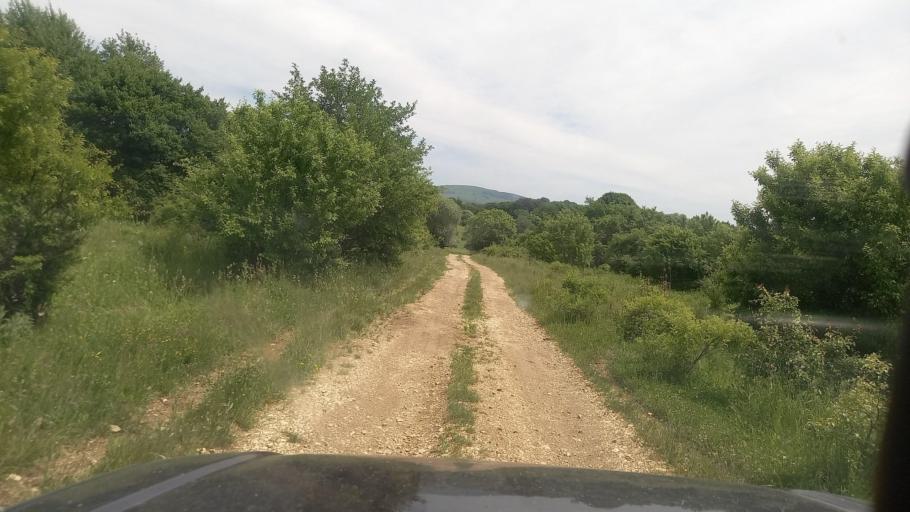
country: RU
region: Karachayevo-Cherkesiya
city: Pregradnaya
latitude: 44.0937
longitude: 41.1657
